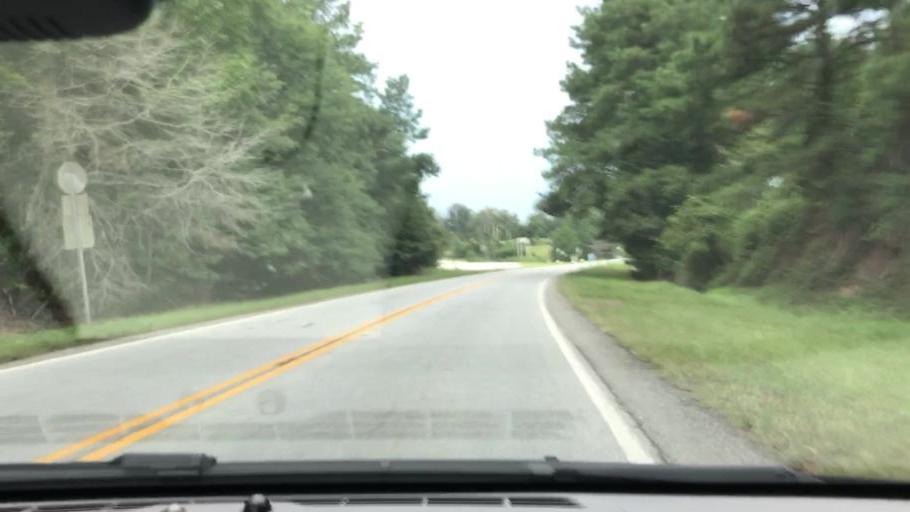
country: US
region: Alabama
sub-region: Houston County
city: Ashford
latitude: 31.2800
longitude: -85.0944
